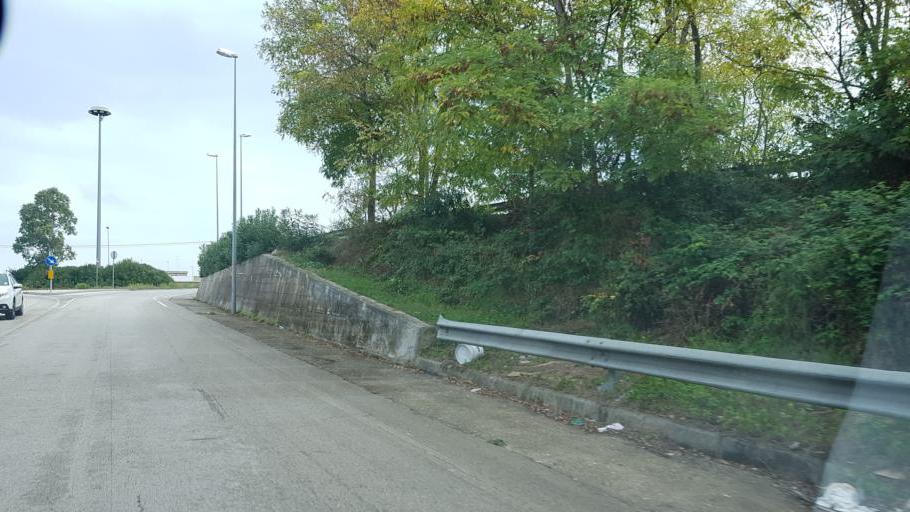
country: IT
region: Apulia
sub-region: Provincia di Bari
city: Triggiano
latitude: 41.0859
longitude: 16.8950
